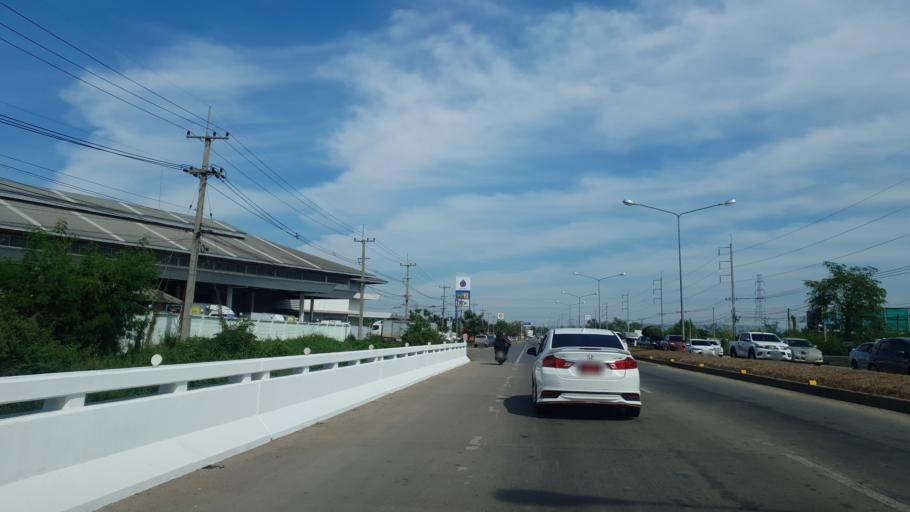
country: TH
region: Phitsanulok
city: Wang Thong
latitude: 16.8552
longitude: 100.3498
